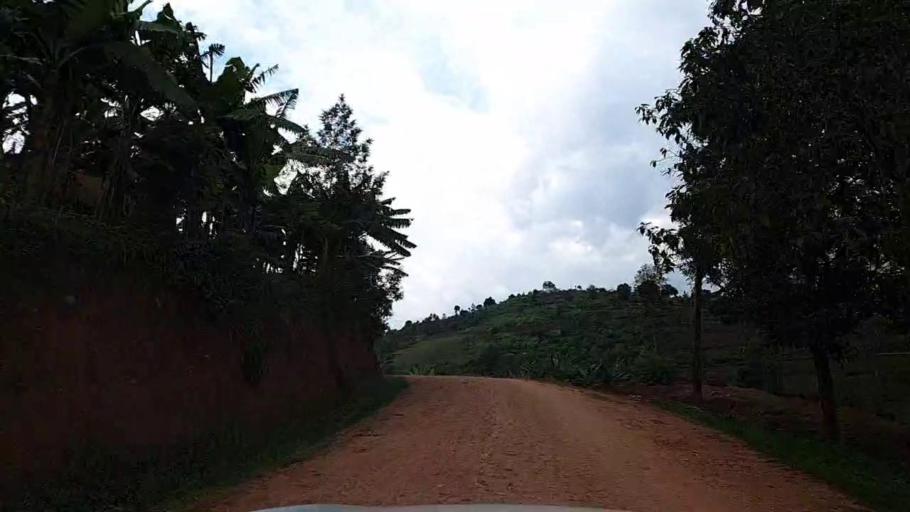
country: RW
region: Southern Province
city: Gikongoro
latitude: -2.4169
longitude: 29.6667
